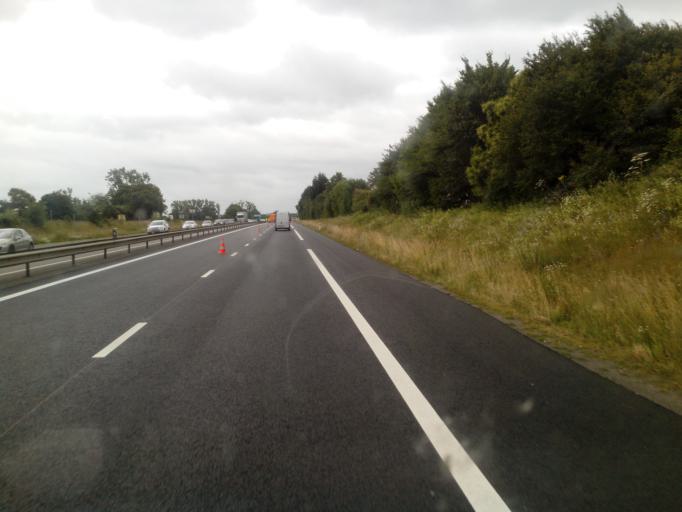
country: FR
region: Brittany
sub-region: Departement d'Ille-et-Vilaine
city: Chatillon-sur-Seiche
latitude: 48.0698
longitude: -1.6768
